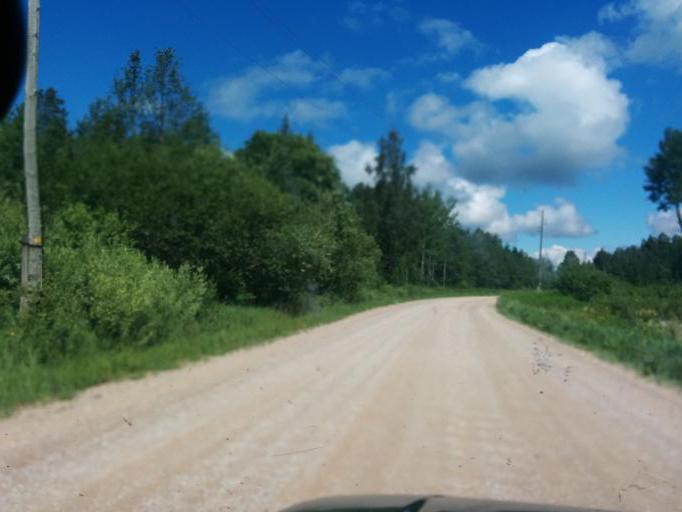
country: LV
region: Vilaka
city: Vilaka
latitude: 57.3595
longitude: 27.4627
